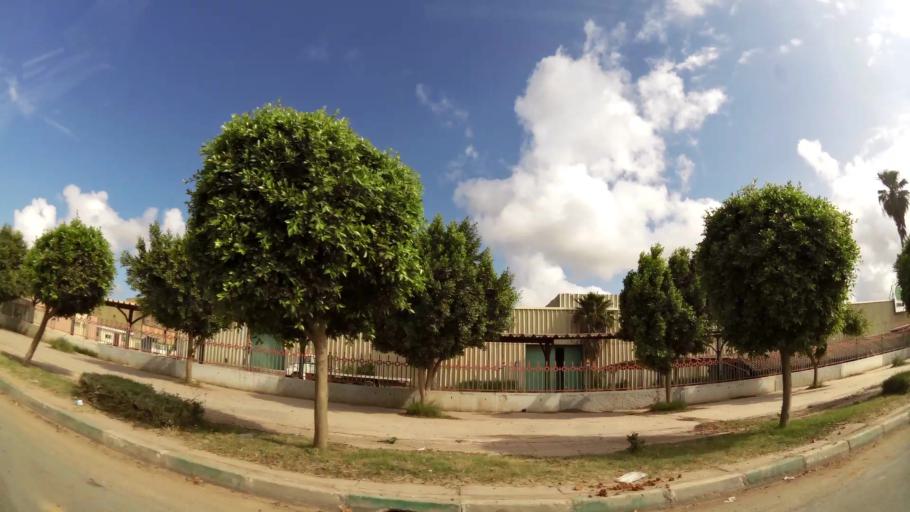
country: MA
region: Gharb-Chrarda-Beni Hssen
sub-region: Kenitra Province
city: Kenitra
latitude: 34.2793
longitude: -6.5444
